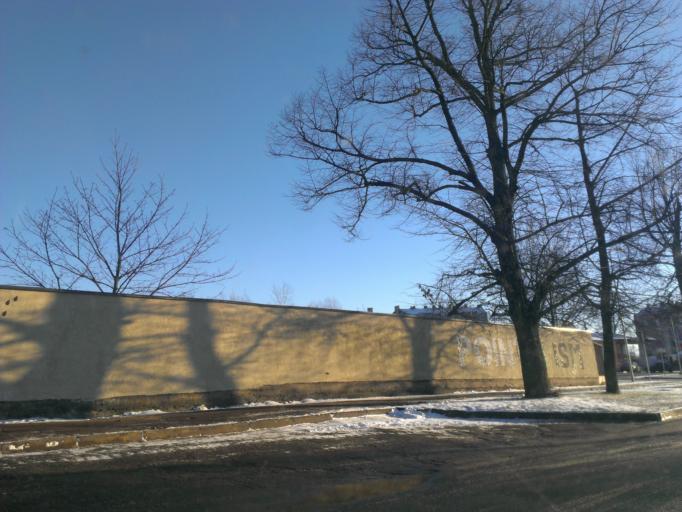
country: LV
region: Riga
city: Riga
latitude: 56.9938
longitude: 24.1208
